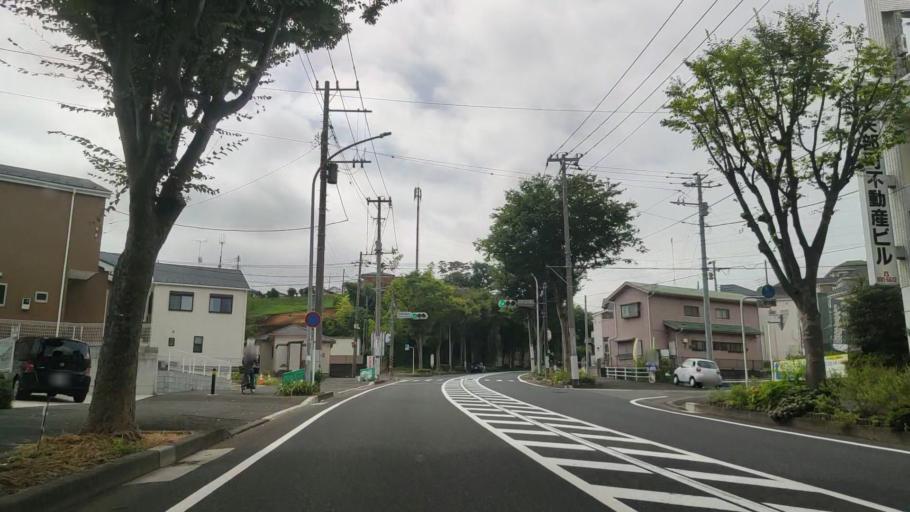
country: JP
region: Kanagawa
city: Minami-rinkan
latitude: 35.4234
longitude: 139.5271
